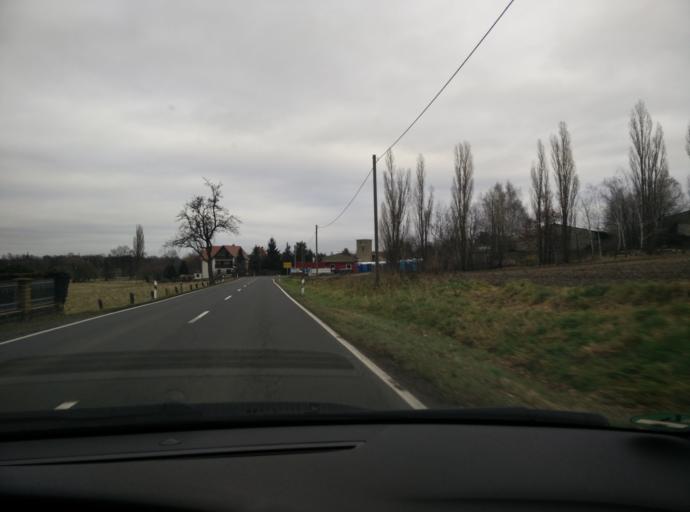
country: DE
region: Saxony
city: Bad Lausick
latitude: 51.1411
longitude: 12.6155
